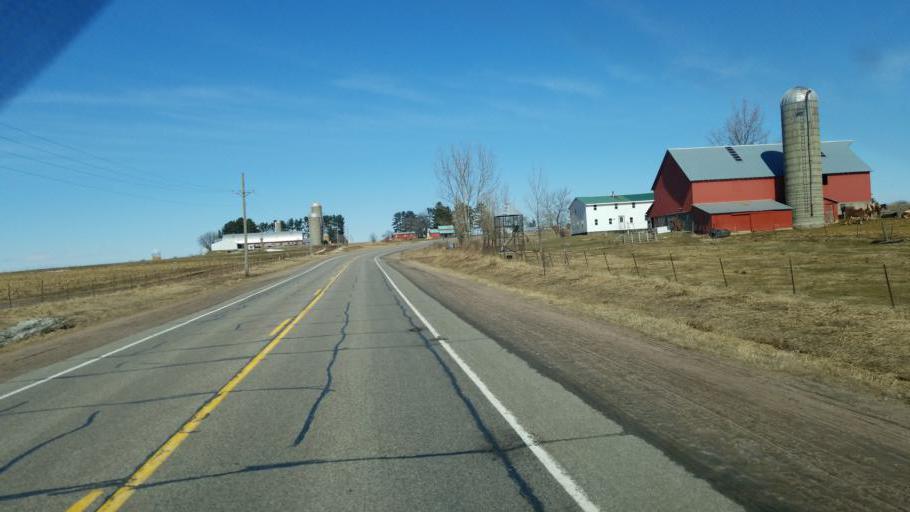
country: US
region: Wisconsin
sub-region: Marathon County
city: Spencer
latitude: 44.5920
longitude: -90.3764
